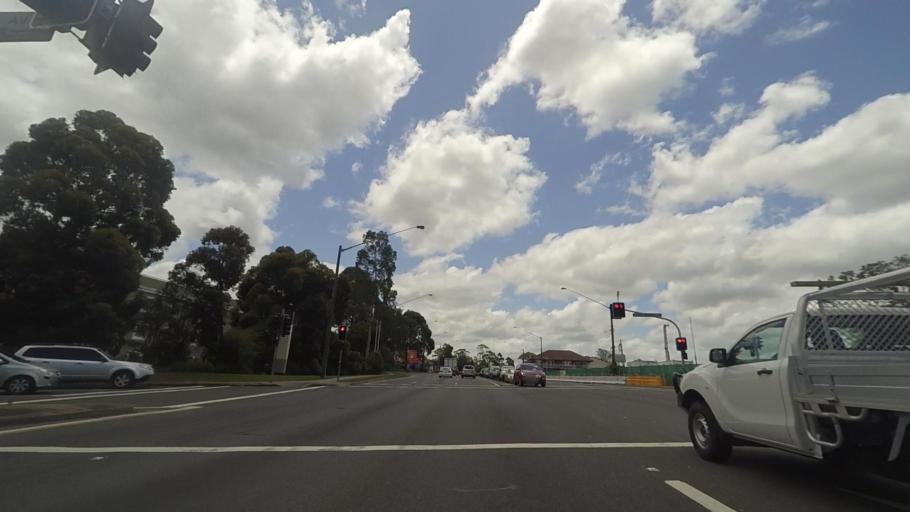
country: AU
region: New South Wales
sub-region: Hornsby Shire
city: Pennant Hills
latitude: -33.7283
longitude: 151.0840
